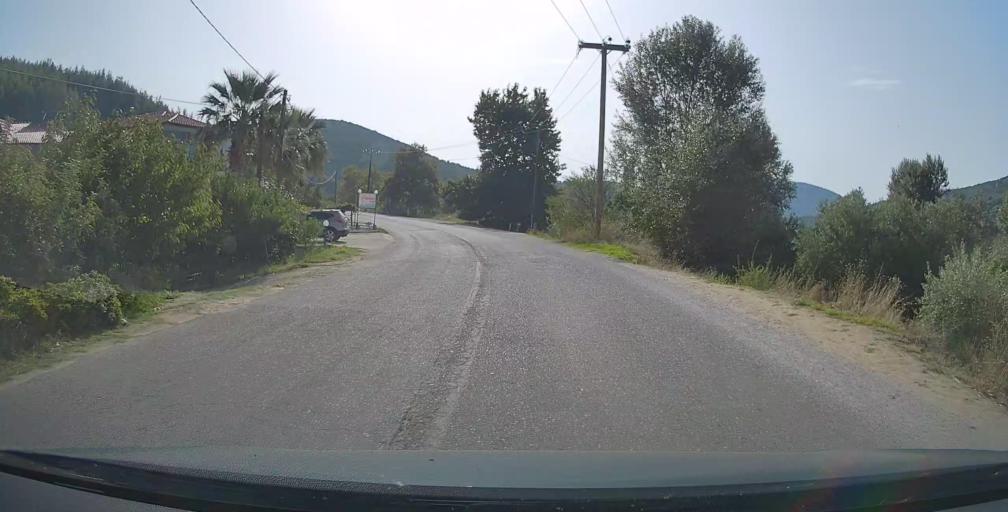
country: GR
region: Central Macedonia
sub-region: Nomos Chalkidikis
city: Sykia
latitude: 39.9625
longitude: 23.9277
